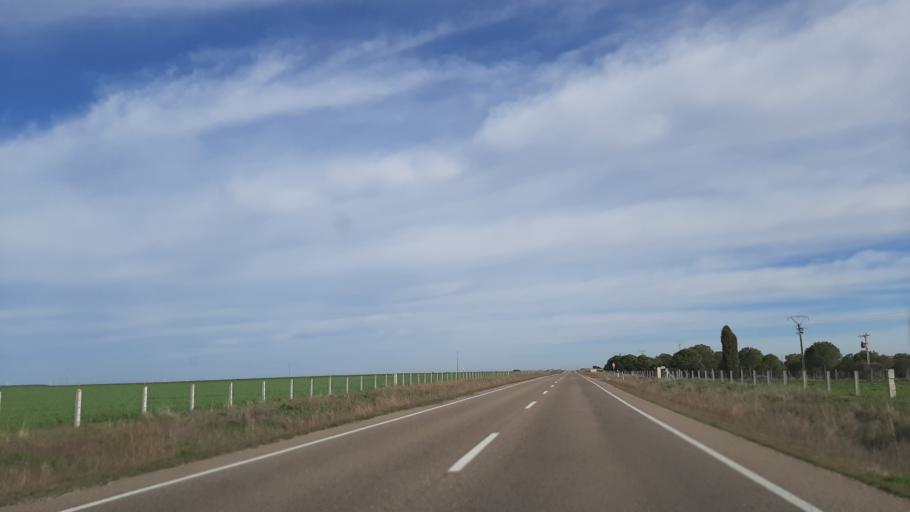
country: ES
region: Castille and Leon
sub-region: Provincia de Salamanca
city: Ledesma
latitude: 41.0900
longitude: -5.9725
